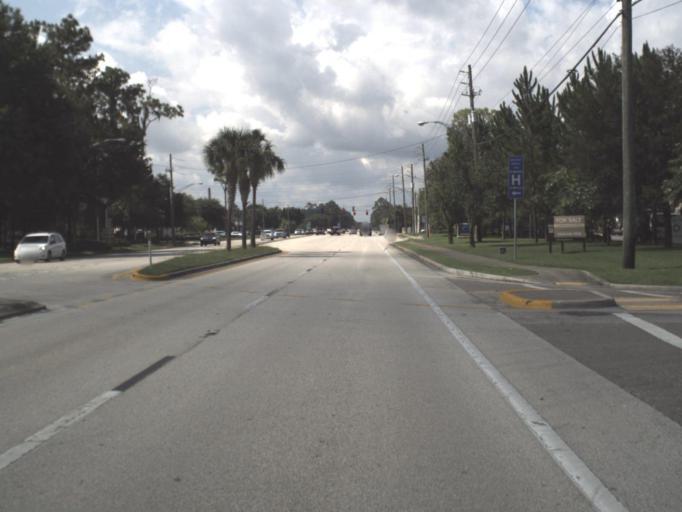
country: US
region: Florida
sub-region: Saint Johns County
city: Fruit Cove
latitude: 30.1238
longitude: -81.6252
